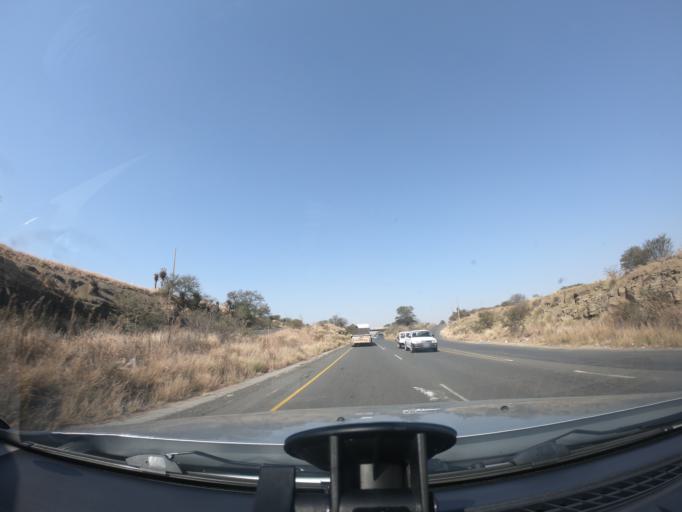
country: ZA
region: KwaZulu-Natal
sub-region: uThukela District Municipality
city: Ladysmith
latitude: -28.7487
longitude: 29.8215
